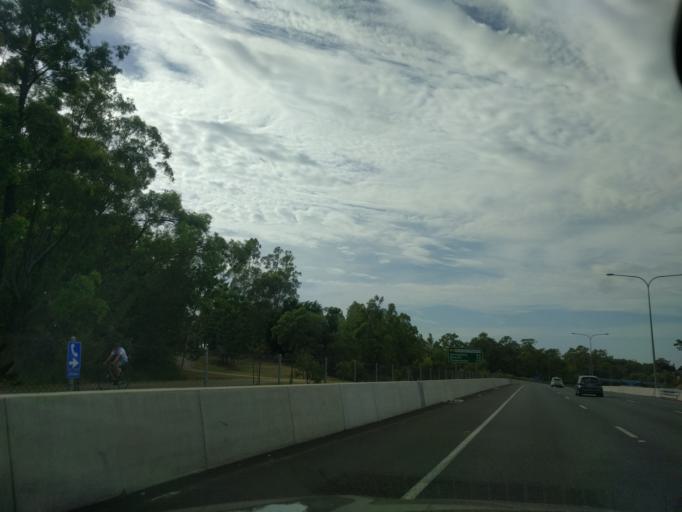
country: AU
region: Queensland
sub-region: Brisbane
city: Taringa
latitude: -27.4887
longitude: 152.9666
